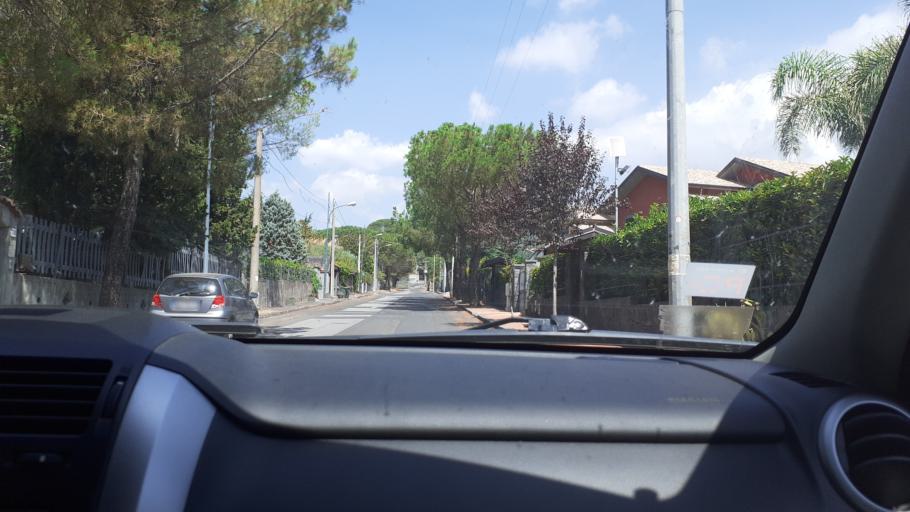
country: IT
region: Sicily
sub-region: Catania
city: Nicolosi
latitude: 37.6226
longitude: 15.0264
